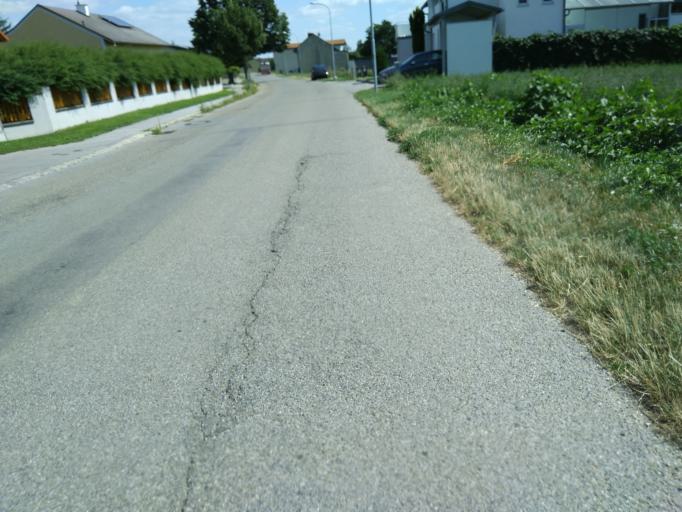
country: AT
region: Lower Austria
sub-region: Politischer Bezirk Mistelbach
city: Wolkersdorf im Weinviertel
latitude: 48.3745
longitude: 16.5157
